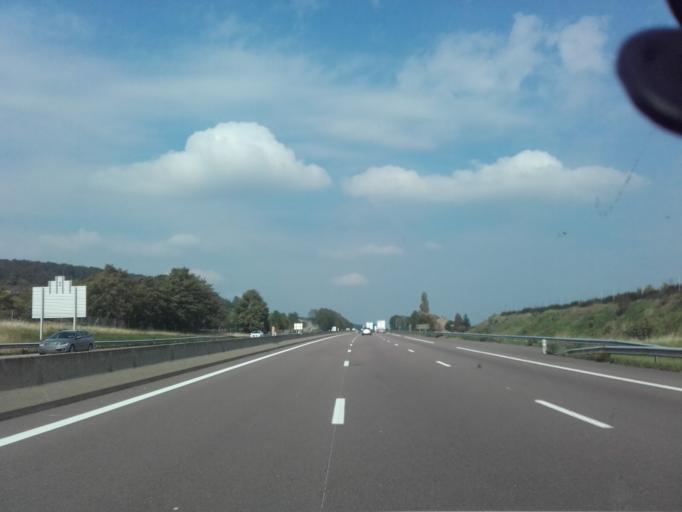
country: FR
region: Bourgogne
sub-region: Departement de Saone-et-Loire
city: Tournus
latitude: 46.5706
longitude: 4.8961
